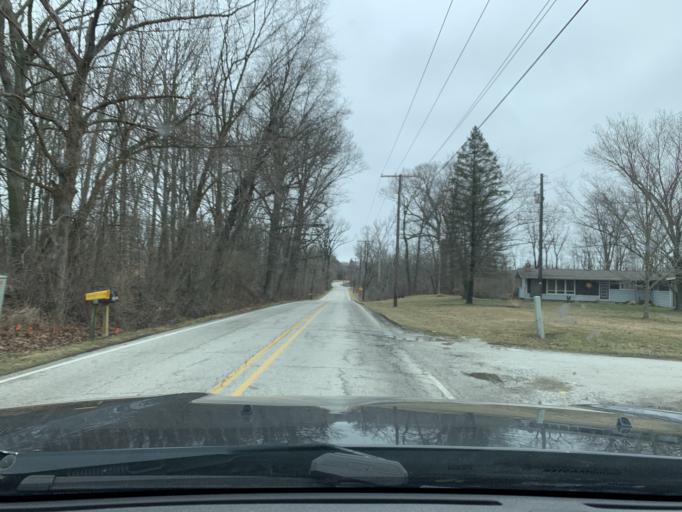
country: US
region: Indiana
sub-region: Porter County
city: Chesterton
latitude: 41.6129
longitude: -87.0165
